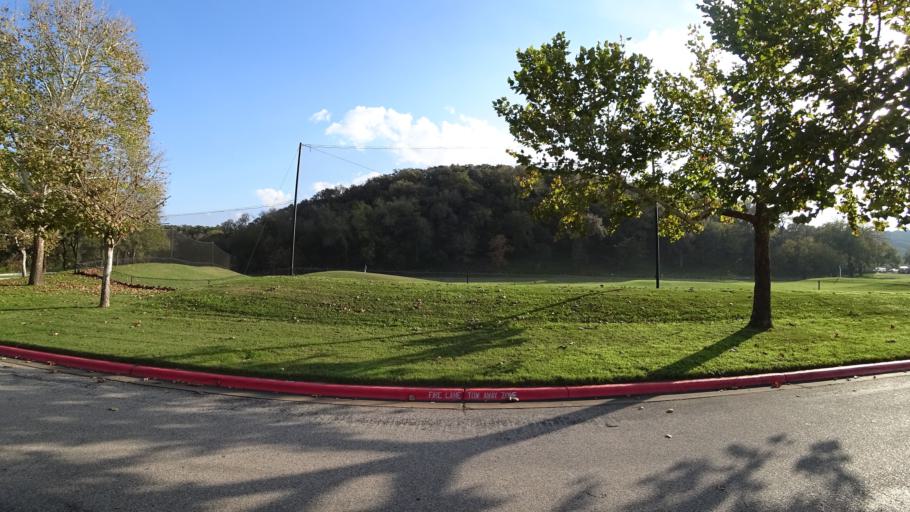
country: US
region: Texas
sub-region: Travis County
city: Lost Creek
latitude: 30.2750
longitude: -97.8469
